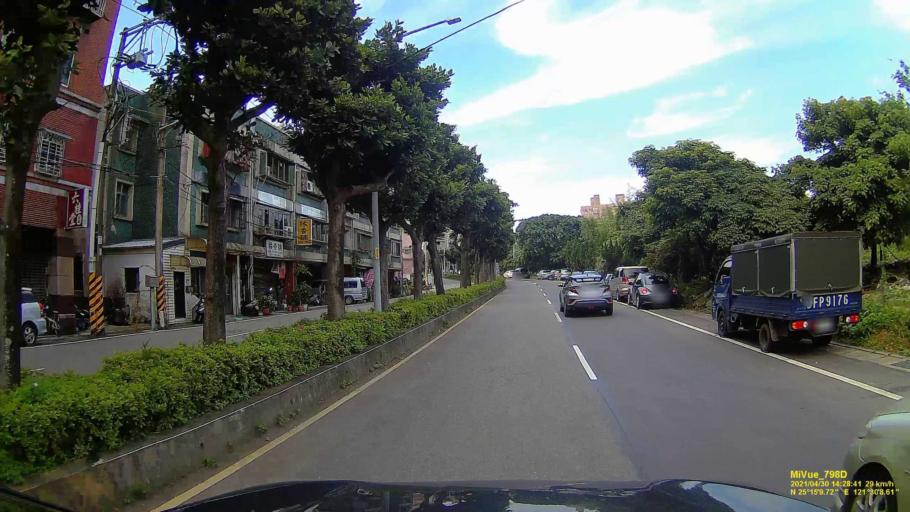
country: TW
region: Taipei
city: Taipei
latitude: 25.2529
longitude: 121.5025
